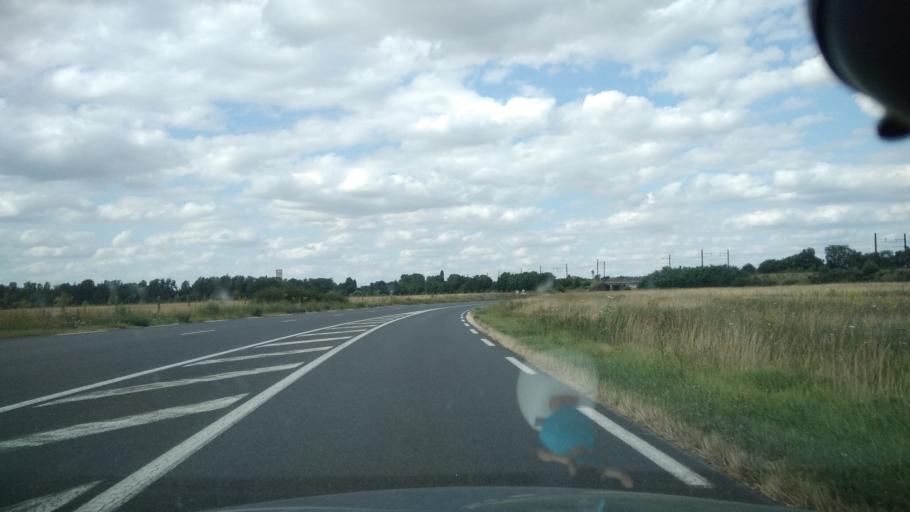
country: FR
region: Centre
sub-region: Departement d'Indre-et-Loire
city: La Celle-Saint-Avant
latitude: 47.0003
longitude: 0.5952
